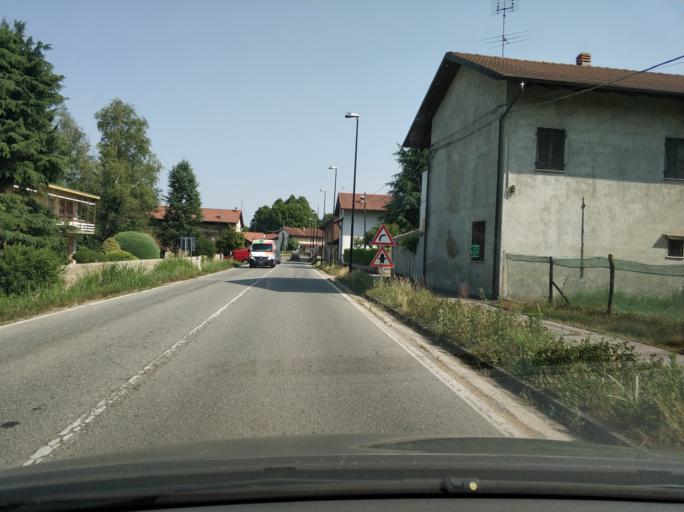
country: IT
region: Piedmont
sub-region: Provincia di Torino
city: Lombardore
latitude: 45.2363
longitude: 7.7404
